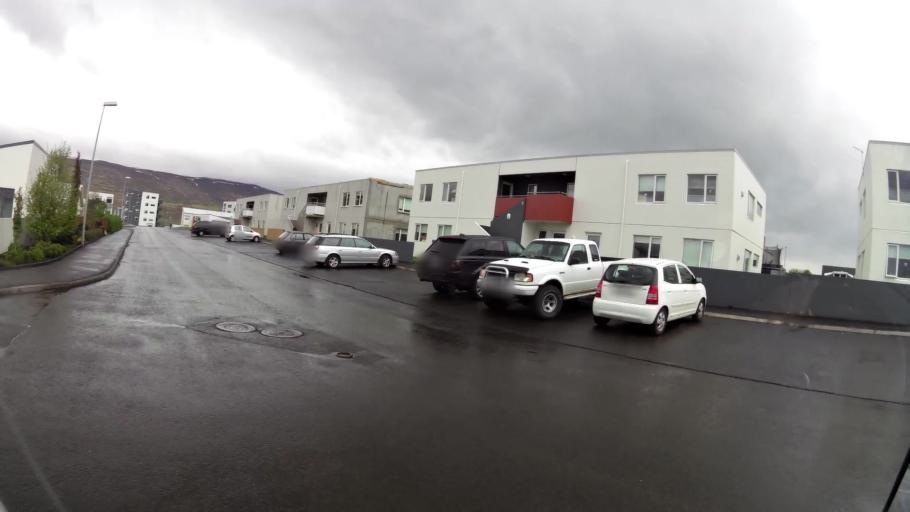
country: IS
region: Northeast
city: Akureyri
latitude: 65.6629
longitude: -18.1034
